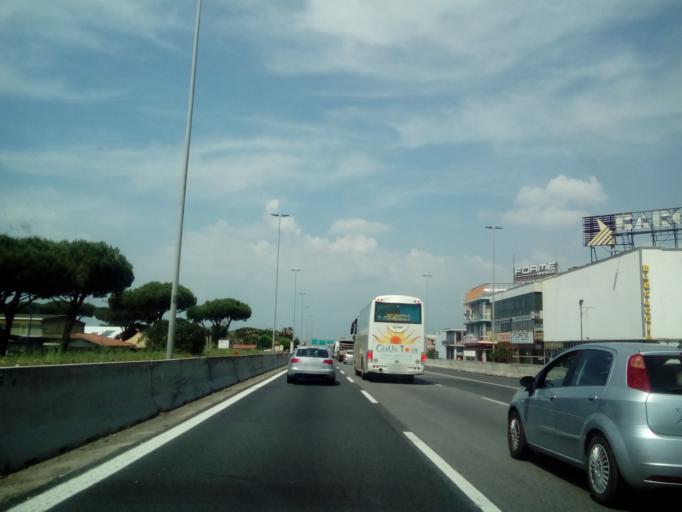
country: IT
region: Latium
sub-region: Citta metropolitana di Roma Capitale
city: Ciampino
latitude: 41.8250
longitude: 12.5821
